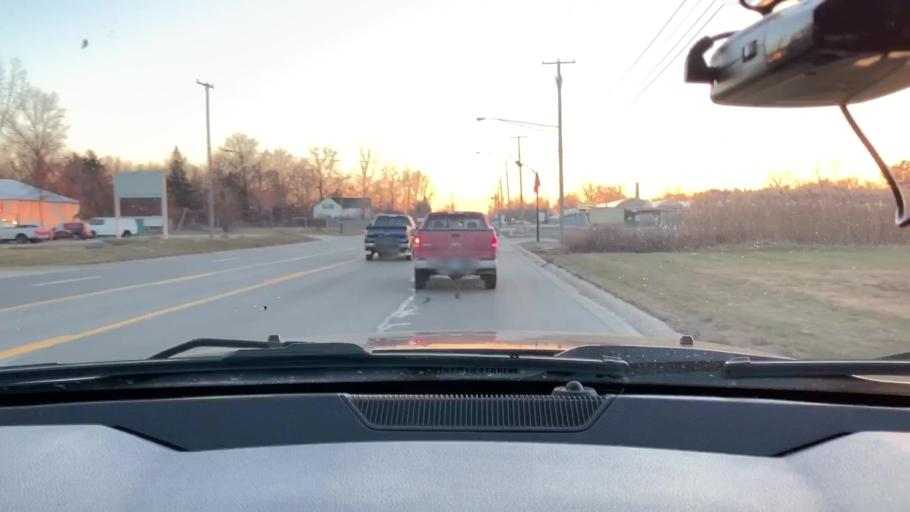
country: US
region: Michigan
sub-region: Wayne County
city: Woodhaven
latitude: 42.1289
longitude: -83.2725
